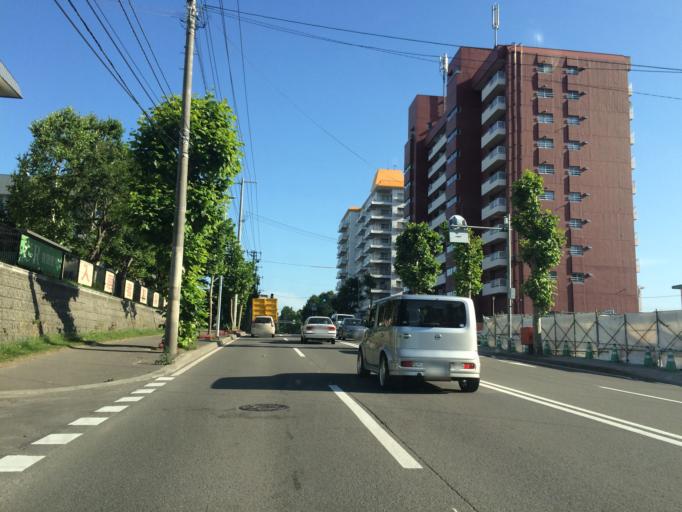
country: JP
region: Hokkaido
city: Sapporo
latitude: 43.0033
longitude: 141.3484
